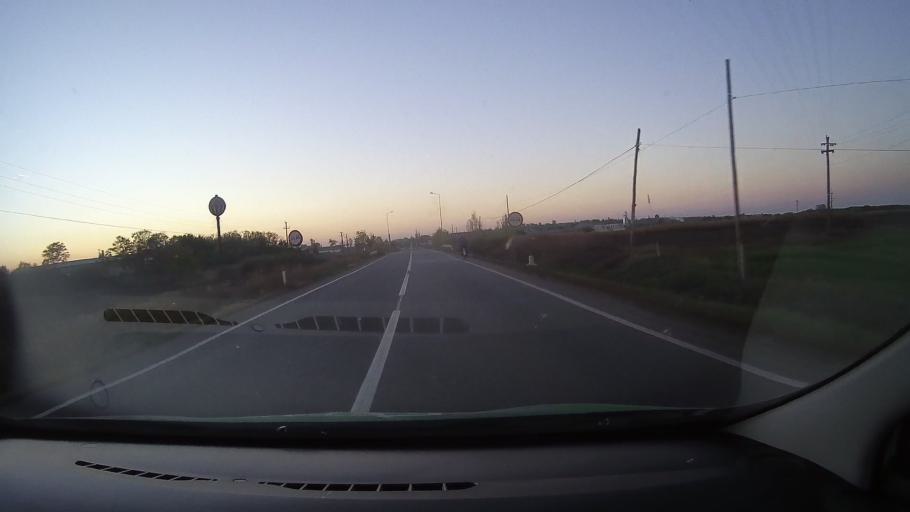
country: RO
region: Bihor
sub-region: Comuna Tarcea
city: Tarcea
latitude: 47.4532
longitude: 22.1810
